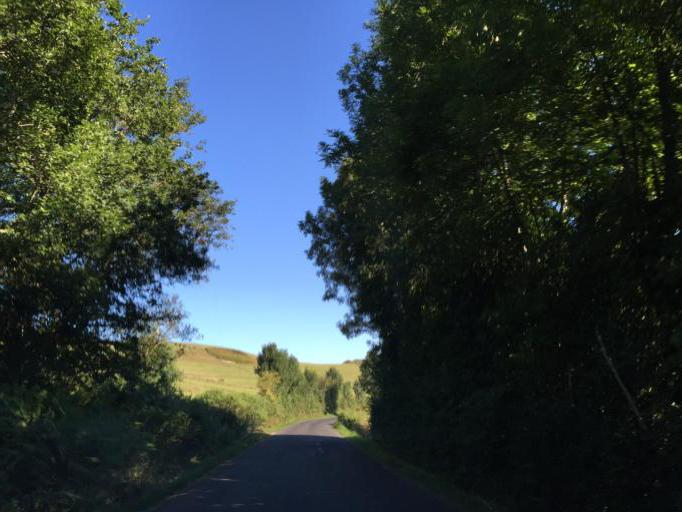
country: FR
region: Midi-Pyrenees
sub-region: Departement de l'Aveyron
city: Laissac
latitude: 44.3353
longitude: 2.7705
